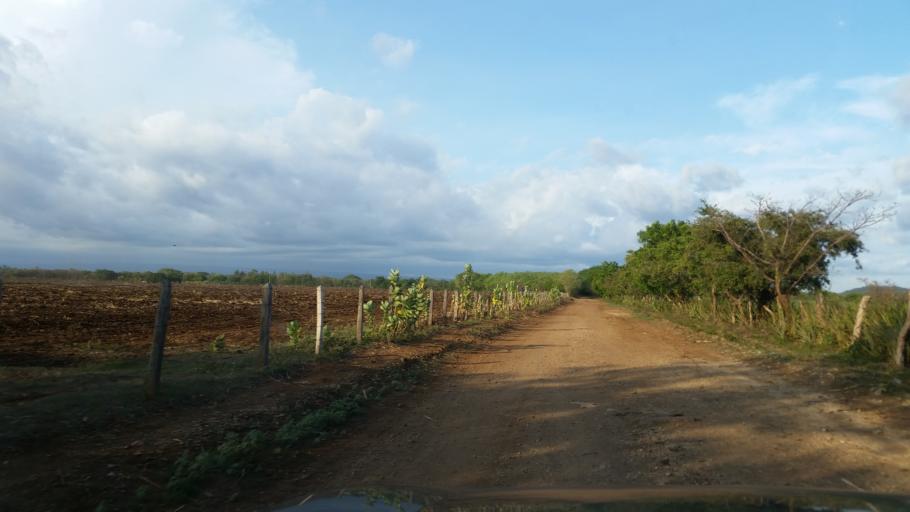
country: NI
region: Managua
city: Masachapa
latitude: 11.7755
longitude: -86.4840
